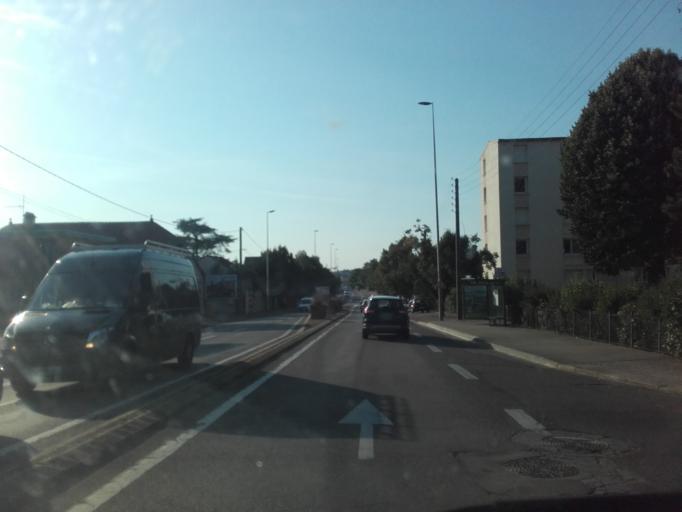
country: FR
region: Bourgogne
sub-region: Departement de l'Yonne
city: Auxerre
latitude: 47.7930
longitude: 3.5873
